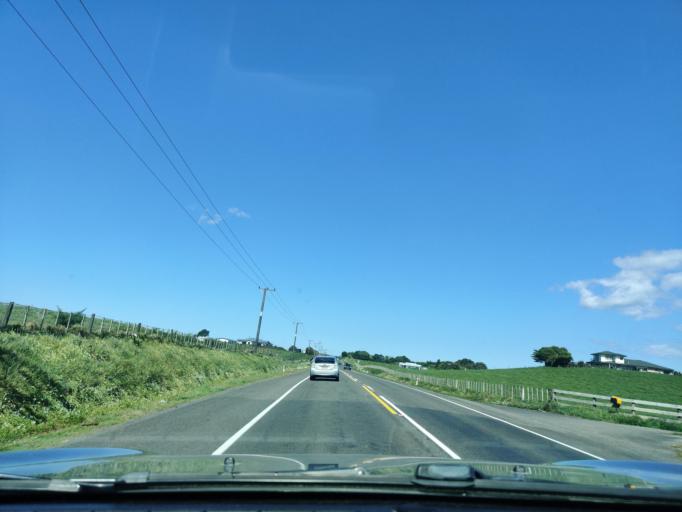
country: NZ
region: Taranaki
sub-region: New Plymouth District
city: New Plymouth
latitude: -39.0966
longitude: 174.0011
